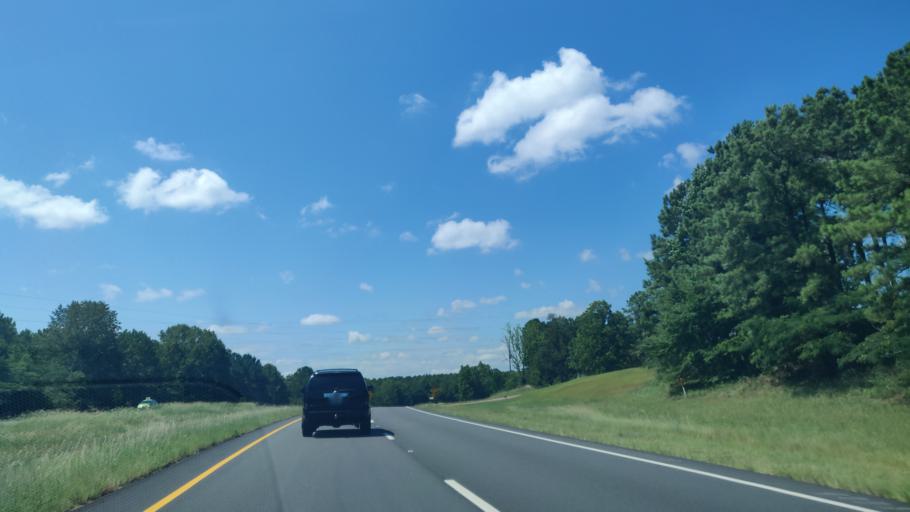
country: US
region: Georgia
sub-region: Stewart County
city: Richland
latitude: 32.1841
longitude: -84.6998
